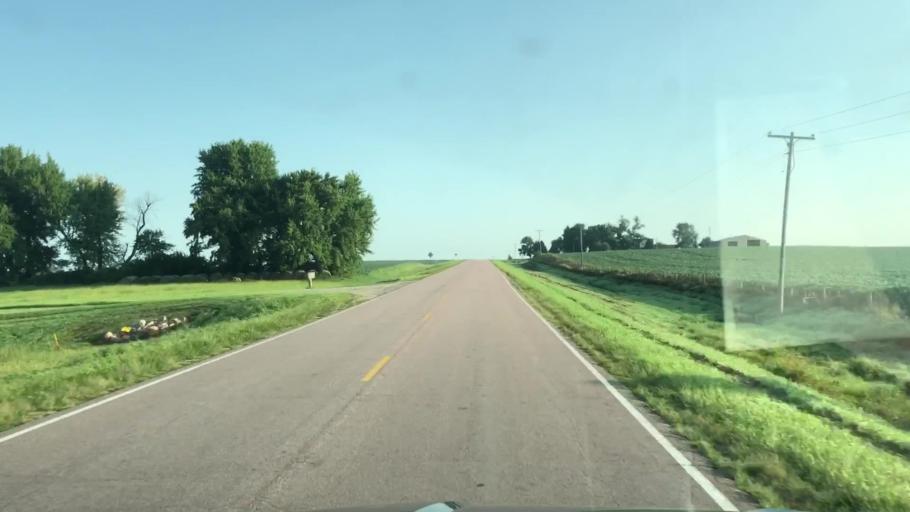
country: US
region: Iowa
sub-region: Lyon County
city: George
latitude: 43.2638
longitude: -96.0000
